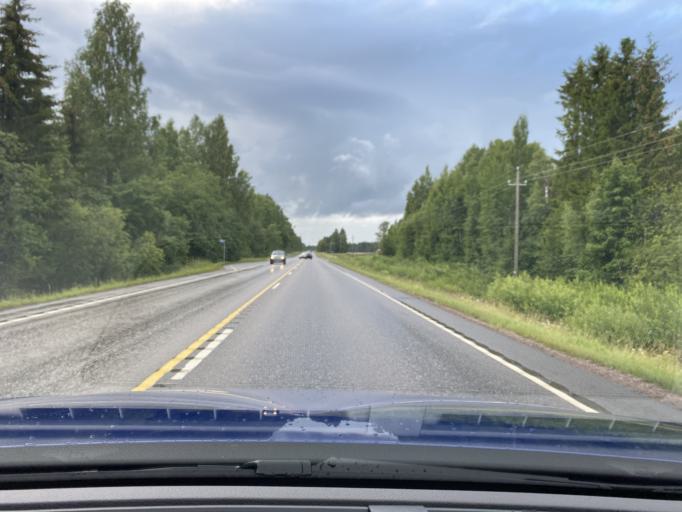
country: FI
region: Uusimaa
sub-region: Helsinki
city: Nurmijaervi
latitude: 60.5427
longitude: 24.8328
